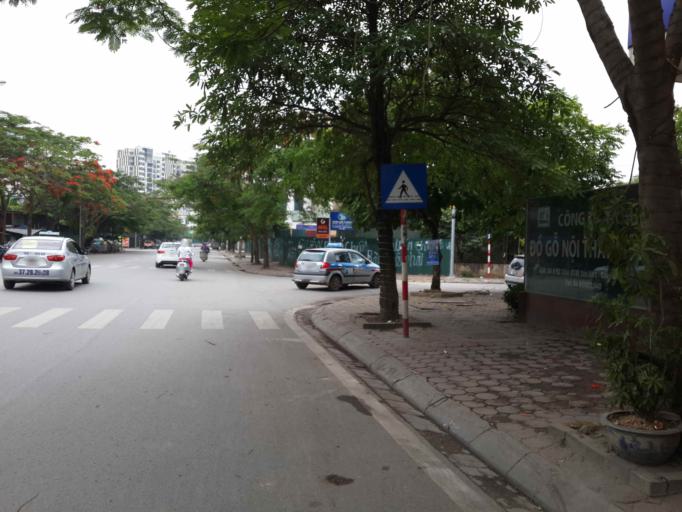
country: VN
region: Ha Noi
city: Cau Giay
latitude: 21.0178
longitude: 105.7972
